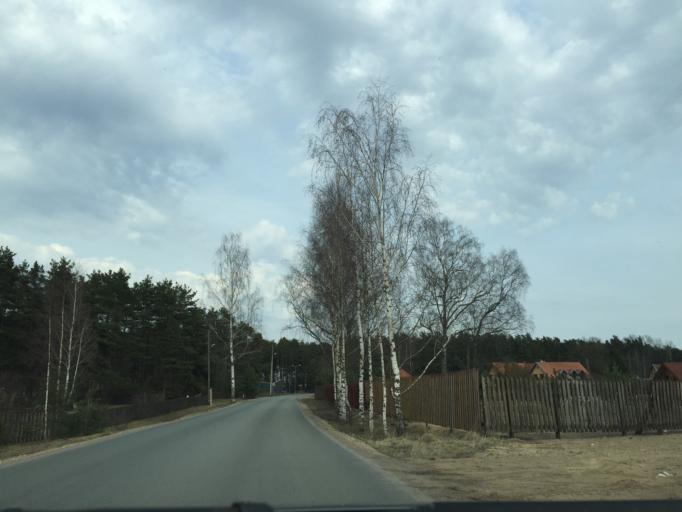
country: LV
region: Kekava
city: Balozi
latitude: 56.8808
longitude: 24.1563
